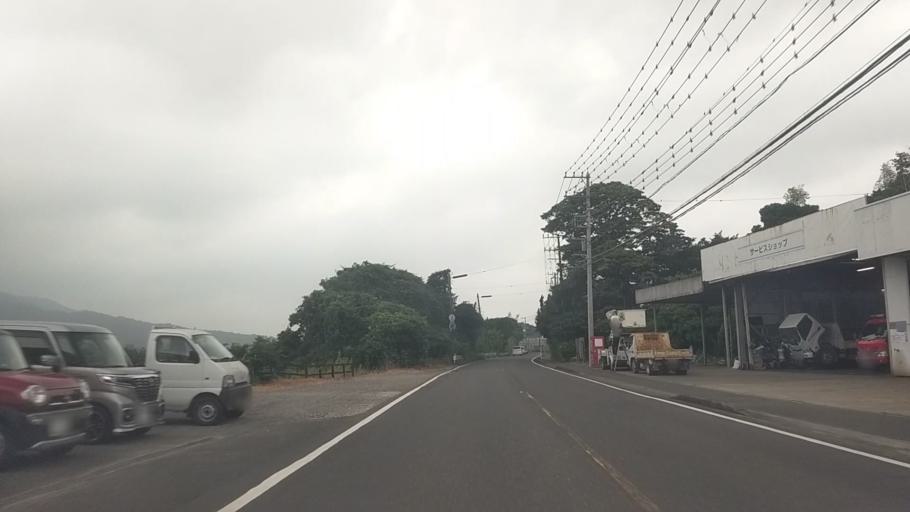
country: JP
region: Chiba
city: Kawaguchi
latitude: 35.1074
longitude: 140.0927
